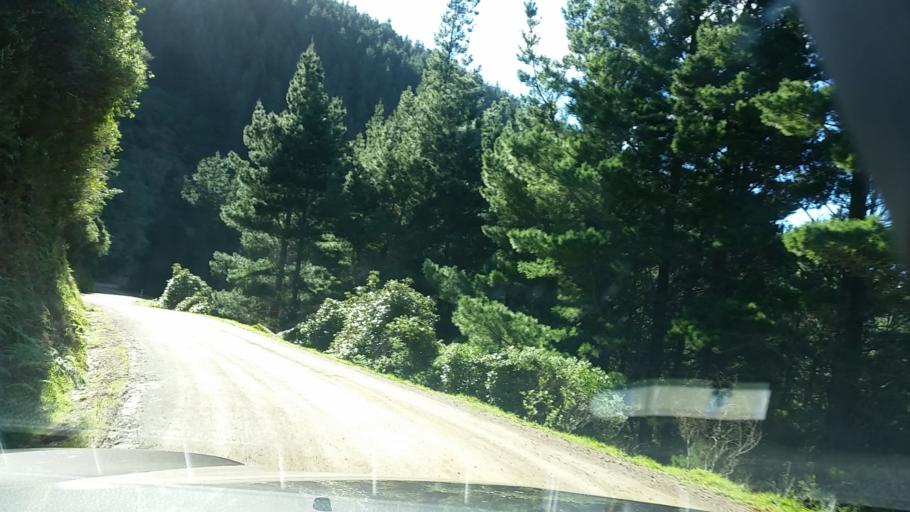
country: NZ
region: Marlborough
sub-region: Marlborough District
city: Picton
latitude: -40.9872
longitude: 173.8143
